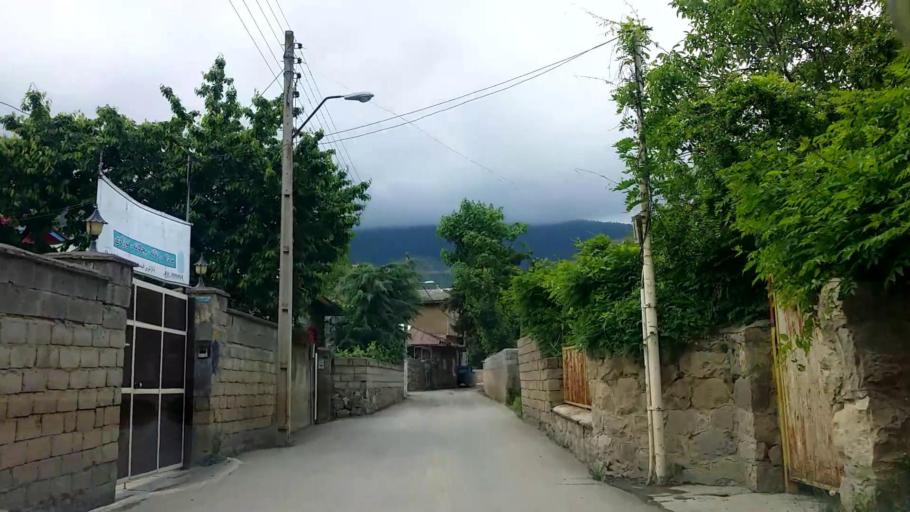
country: IR
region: Mazandaran
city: `Abbasabad
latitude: 36.5015
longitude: 51.1529
